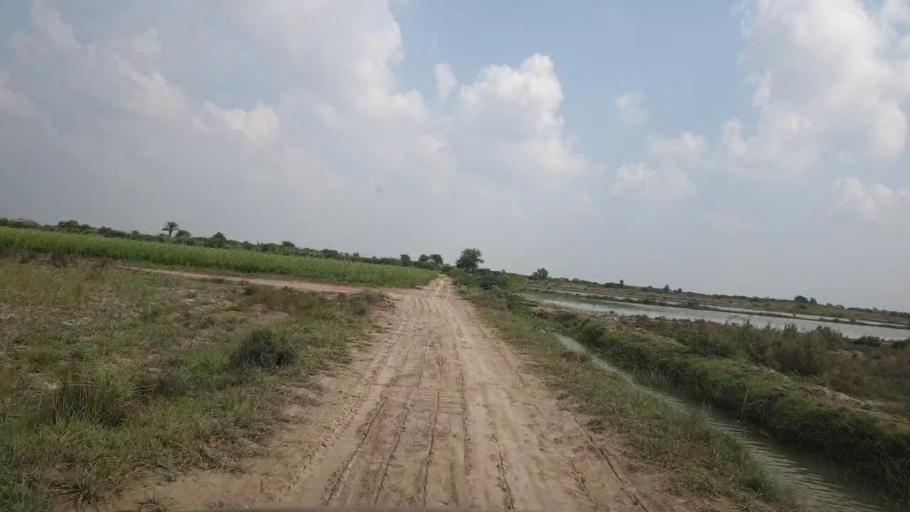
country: PK
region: Sindh
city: Badin
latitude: 24.5328
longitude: 68.6394
